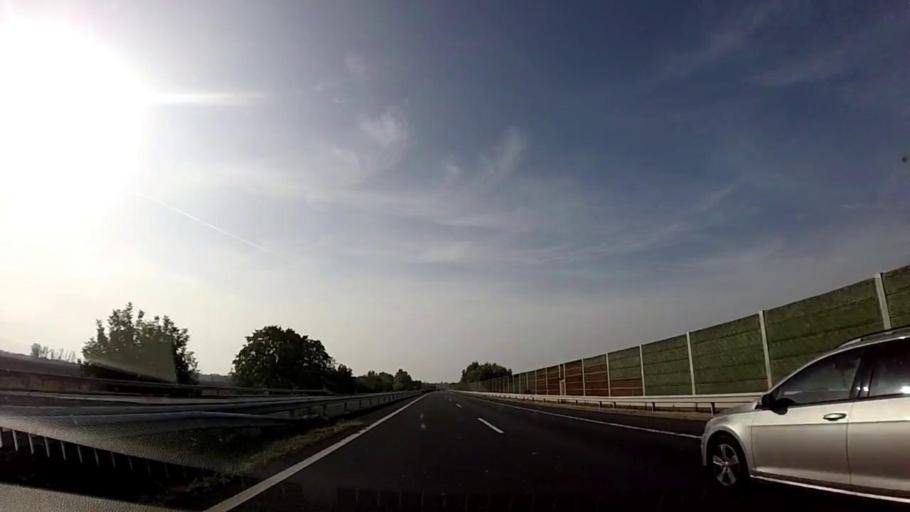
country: HU
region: Somogy
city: Balatonszabadi
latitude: 46.9445
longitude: 18.1483
